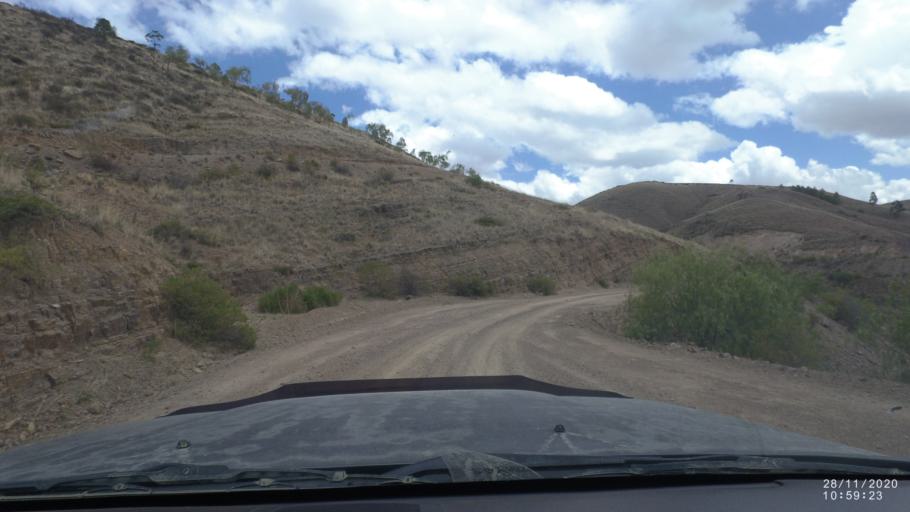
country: BO
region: Cochabamba
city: Capinota
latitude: -17.7734
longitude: -66.1080
